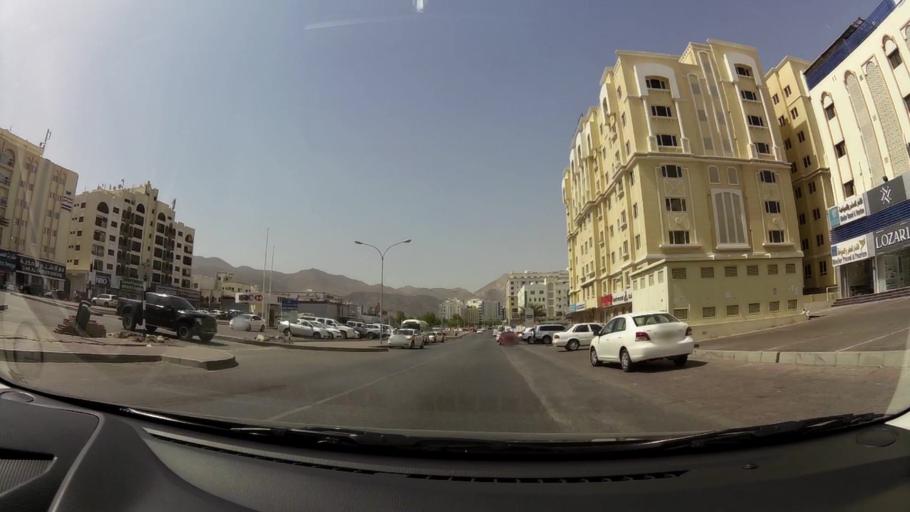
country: OM
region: Muhafazat Masqat
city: Bawshar
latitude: 23.5916
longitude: 58.4282
